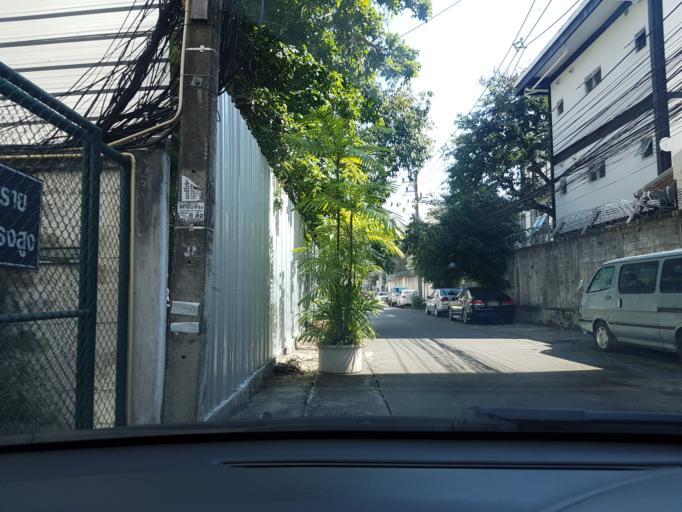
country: TH
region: Chiang Mai
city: Chiang Mai
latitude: 18.7962
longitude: 98.9648
